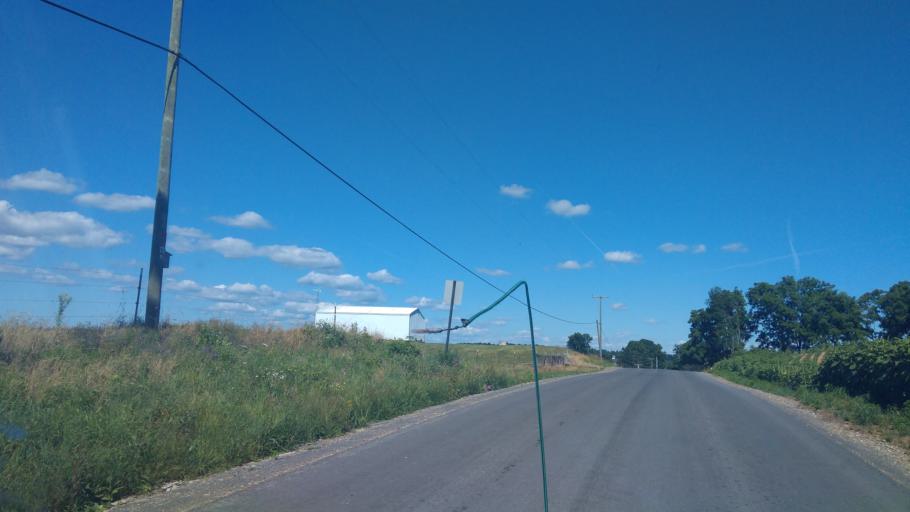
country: US
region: New York
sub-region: Wayne County
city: Clyde
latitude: 43.0259
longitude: -76.8999
